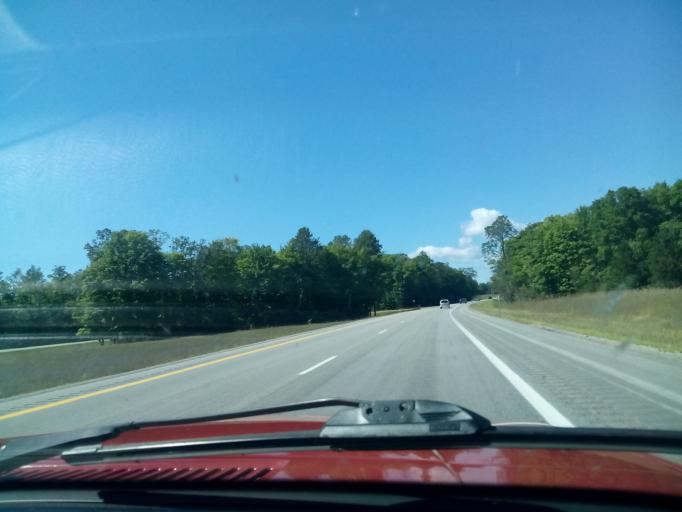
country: US
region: Michigan
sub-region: Cheboygan County
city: Indian River
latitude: 45.3226
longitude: -84.6006
